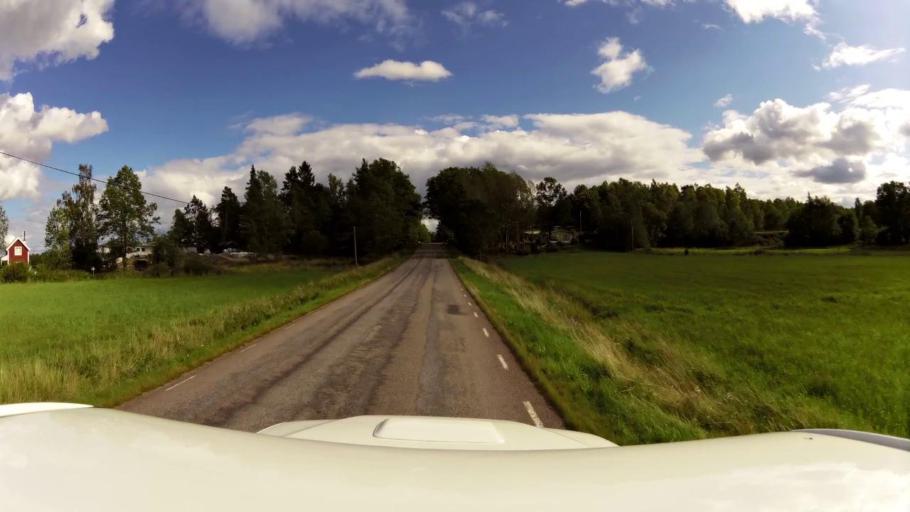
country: SE
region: OEstergoetland
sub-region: Kinda Kommun
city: Rimforsa
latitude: 58.2304
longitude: 15.6929
